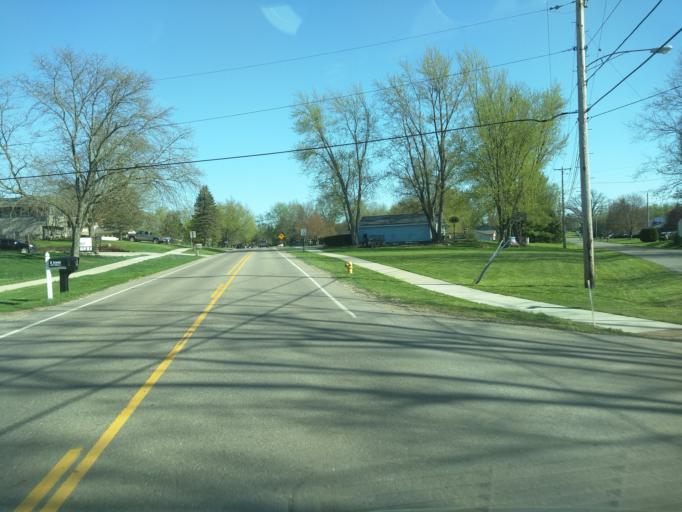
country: US
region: Michigan
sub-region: Eaton County
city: Waverly
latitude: 42.7589
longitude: -84.6474
